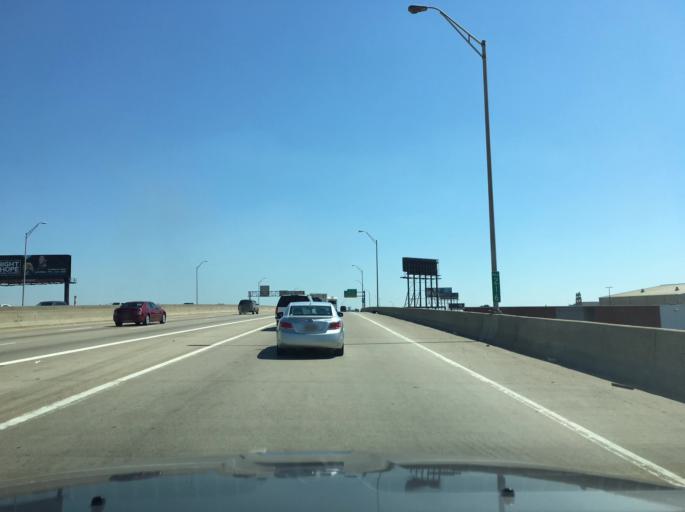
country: US
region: Michigan
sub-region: Wayne County
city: Hamtramck
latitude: 42.3698
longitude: -83.0558
